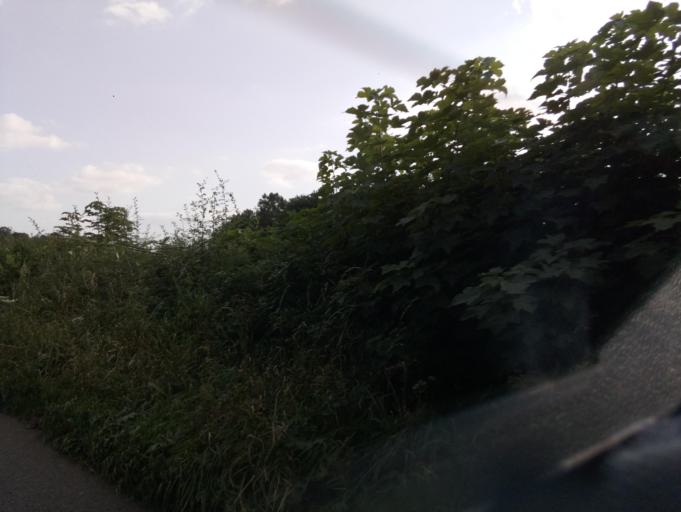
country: GB
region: England
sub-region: Devon
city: Tiverton
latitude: 50.8394
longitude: -3.5018
